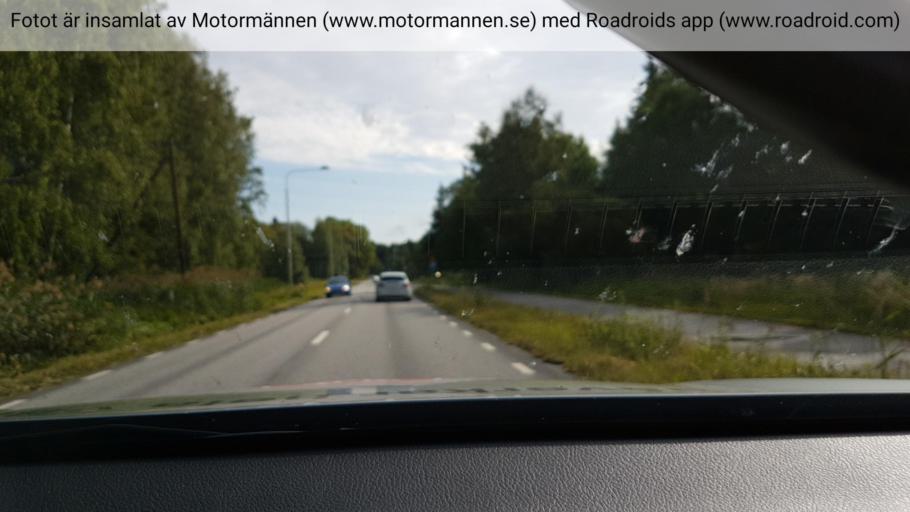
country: SE
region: Stockholm
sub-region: Osterakers Kommun
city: Akersberga
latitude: 59.4997
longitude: 18.3432
